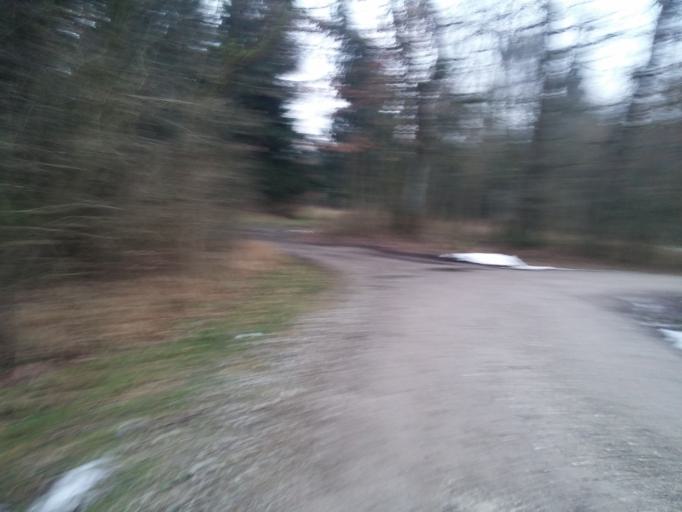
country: DE
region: Bavaria
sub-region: Upper Bavaria
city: Putzbrunn
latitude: 48.0646
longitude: 11.7200
